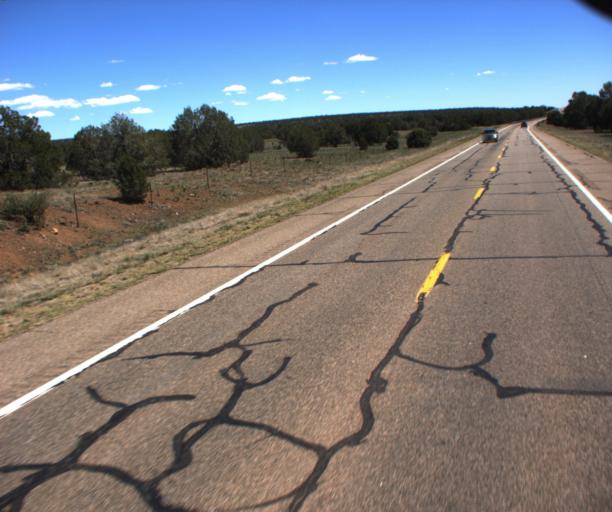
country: US
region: Arizona
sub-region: Yavapai County
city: Paulden
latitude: 35.1272
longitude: -112.4369
